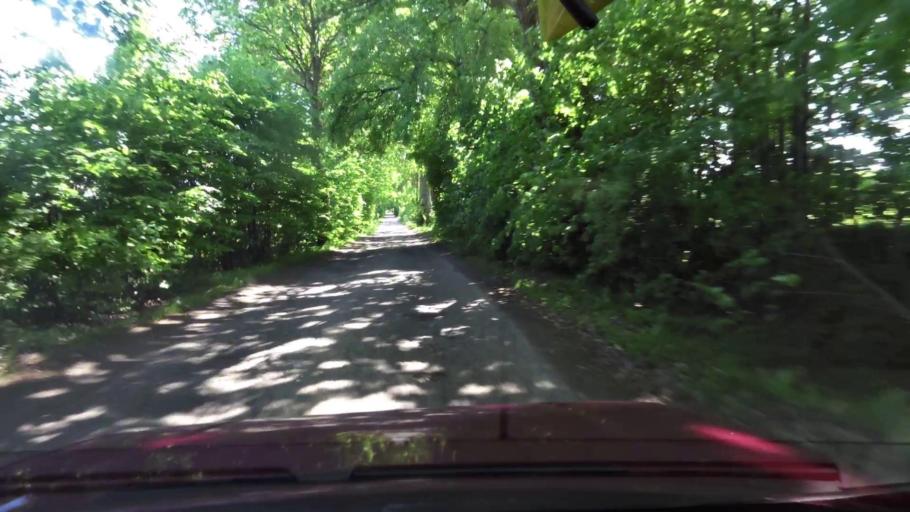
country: PL
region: West Pomeranian Voivodeship
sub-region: Powiat koszalinski
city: Bobolice
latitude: 54.0132
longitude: 16.6577
